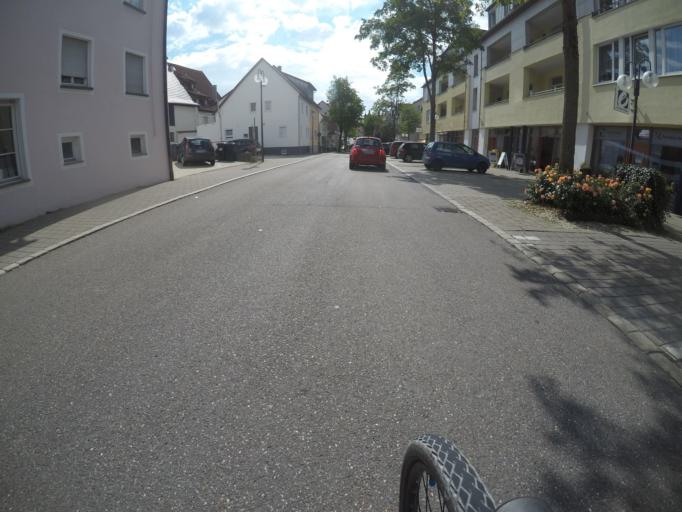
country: DE
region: Baden-Wuerttemberg
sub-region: Tuebingen Region
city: Munsingen
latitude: 48.4134
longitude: 9.4937
